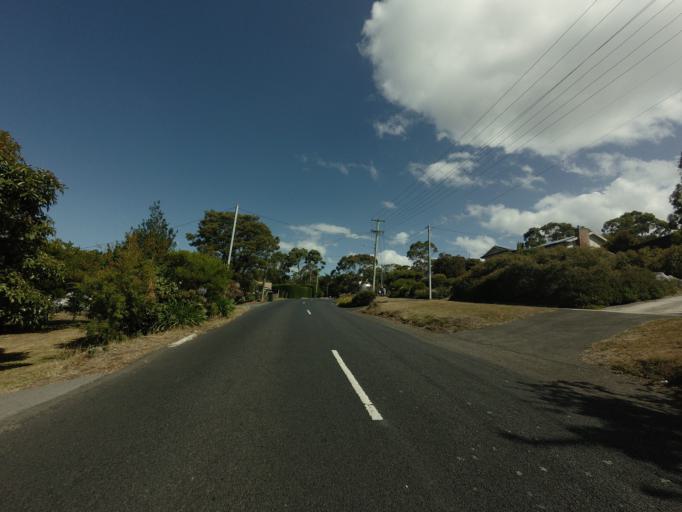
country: AU
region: Tasmania
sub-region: Hobart
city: Dynnyrne
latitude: -42.9165
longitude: 147.3241
